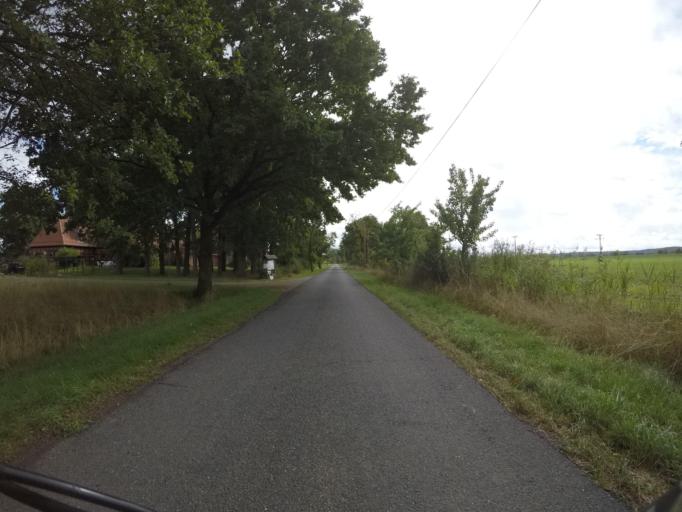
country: DE
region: Lower Saxony
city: Neu Darchau
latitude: 53.2600
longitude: 10.8561
